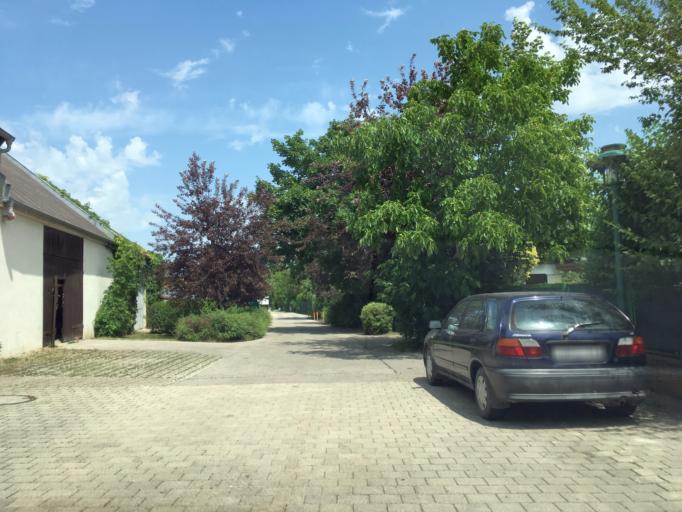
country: AT
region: Lower Austria
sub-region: Politischer Bezirk Baden
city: Tattendorf
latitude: 47.9581
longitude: 16.3022
